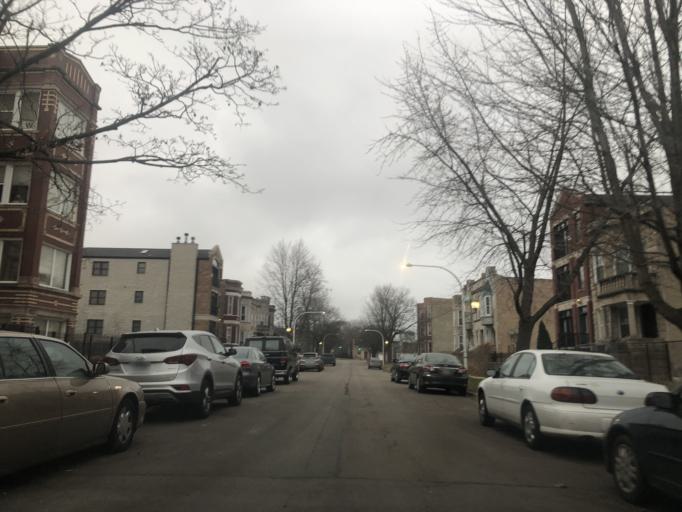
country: US
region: Illinois
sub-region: Cook County
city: Chicago
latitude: 41.7788
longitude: -87.6004
